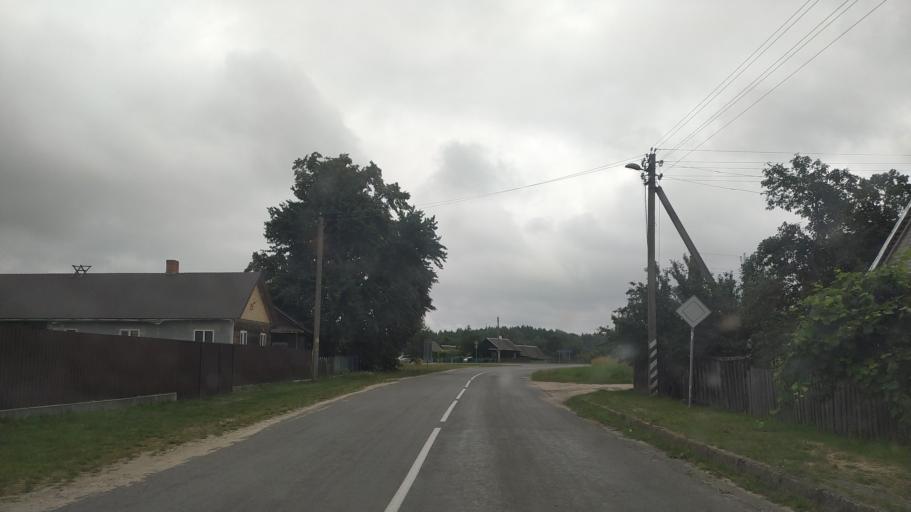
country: BY
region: Brest
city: Byaroza
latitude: 52.5946
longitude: 24.8708
